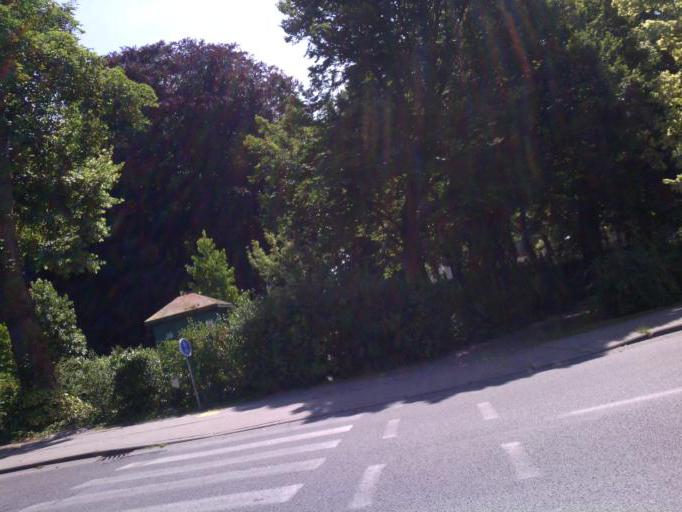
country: BE
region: Wallonia
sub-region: Province du Hainaut
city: Tournai
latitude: 50.6130
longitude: 3.3795
